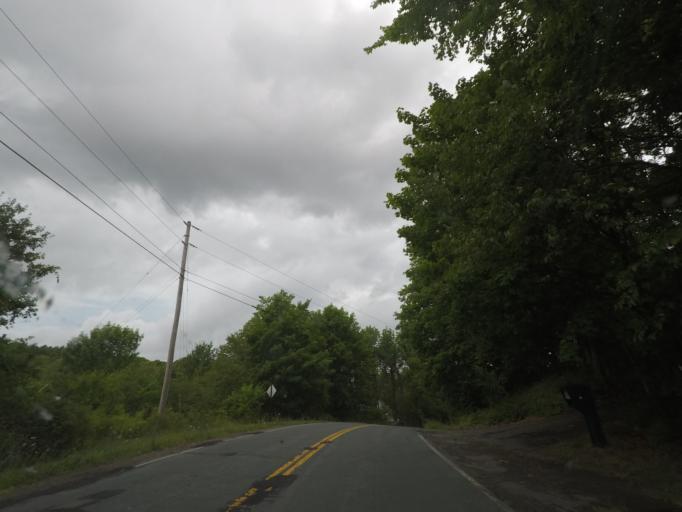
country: US
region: New York
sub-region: Rensselaer County
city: Wynantskill
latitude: 42.6811
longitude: -73.6344
